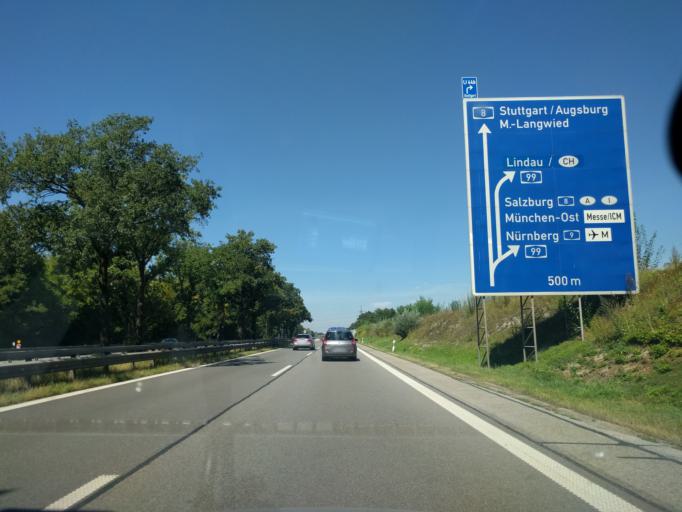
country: DE
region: Bavaria
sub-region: Upper Bavaria
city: Pasing
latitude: 48.1735
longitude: 11.4445
